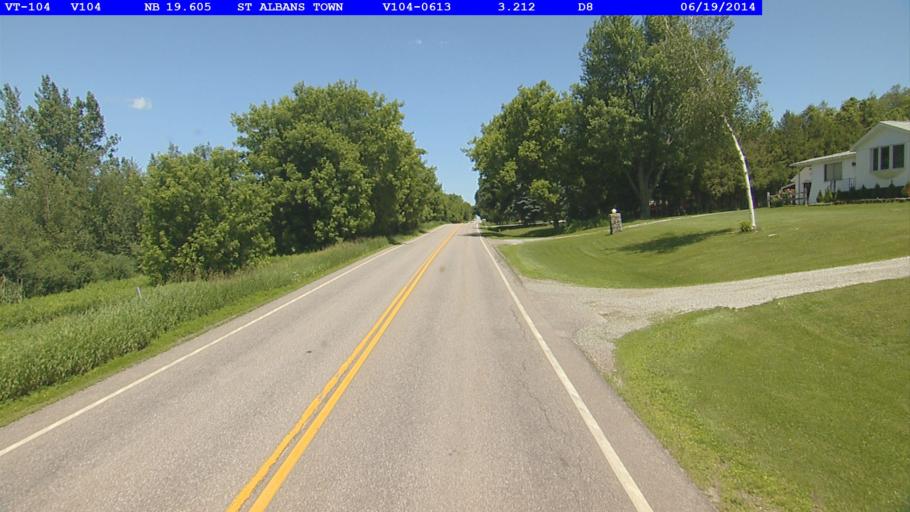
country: US
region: Vermont
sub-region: Franklin County
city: Saint Albans
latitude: 44.8170
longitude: -73.0599
